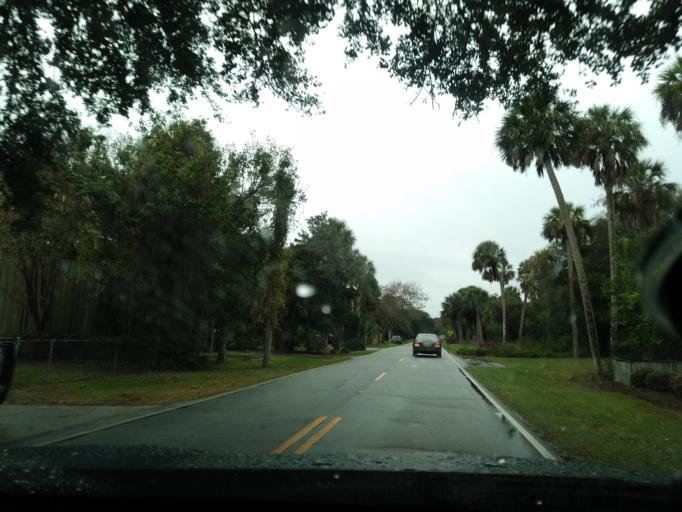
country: US
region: South Carolina
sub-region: Charleston County
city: Folly Beach
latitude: 32.6618
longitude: -79.9261
